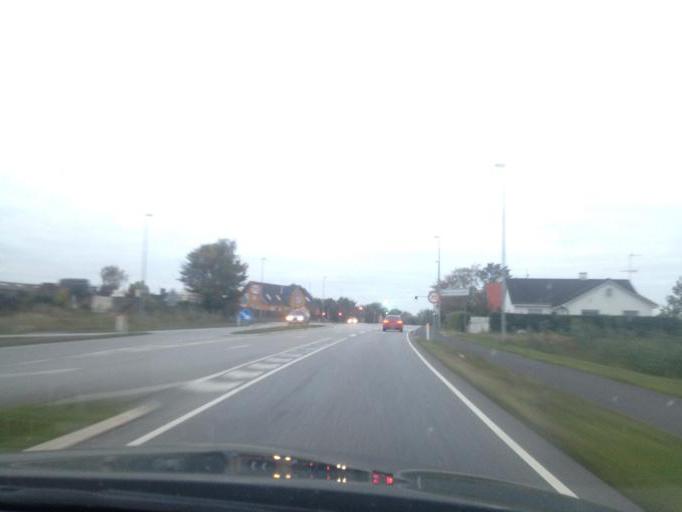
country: DK
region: Zealand
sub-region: Solrod Kommune
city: Havdrup
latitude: 55.5708
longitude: 12.1146
